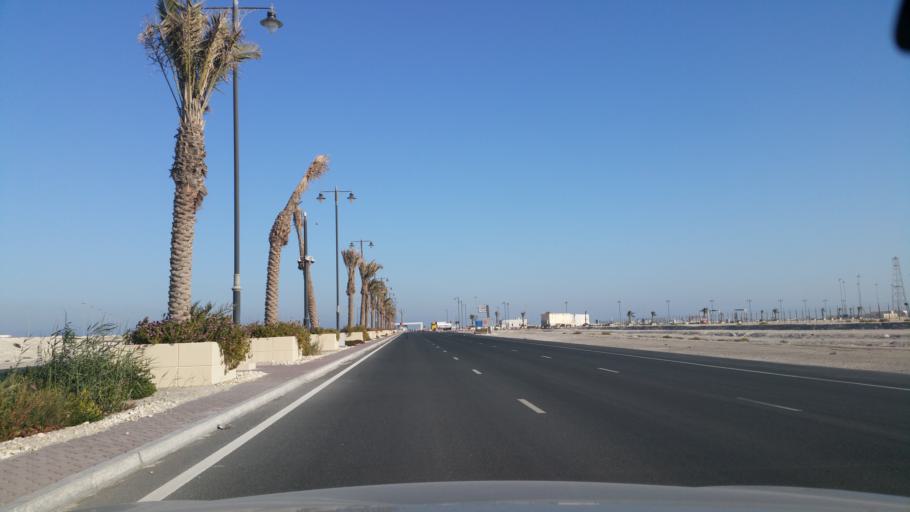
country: QA
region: Al Wakrah
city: Umm Sa'id
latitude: 25.0560
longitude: 51.5989
